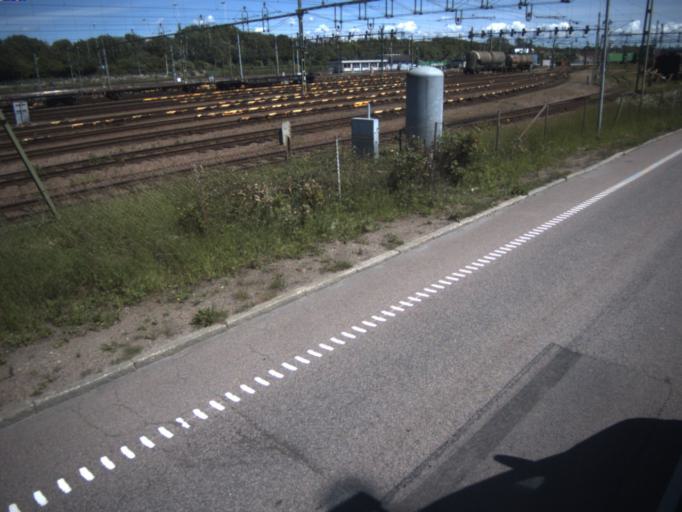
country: SE
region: Skane
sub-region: Helsingborg
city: Helsingborg
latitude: 56.0251
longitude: 12.7222
